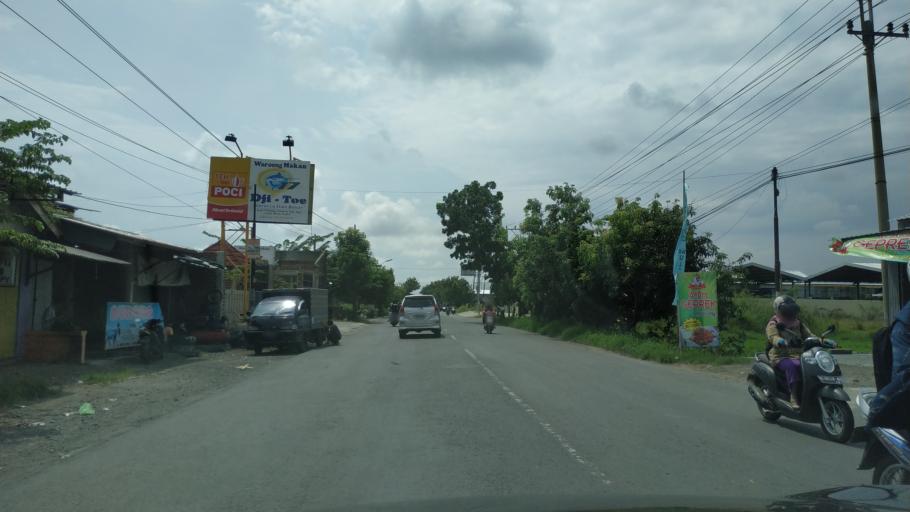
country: ID
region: Central Java
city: Adiwerna
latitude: -6.9294
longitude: 109.1256
